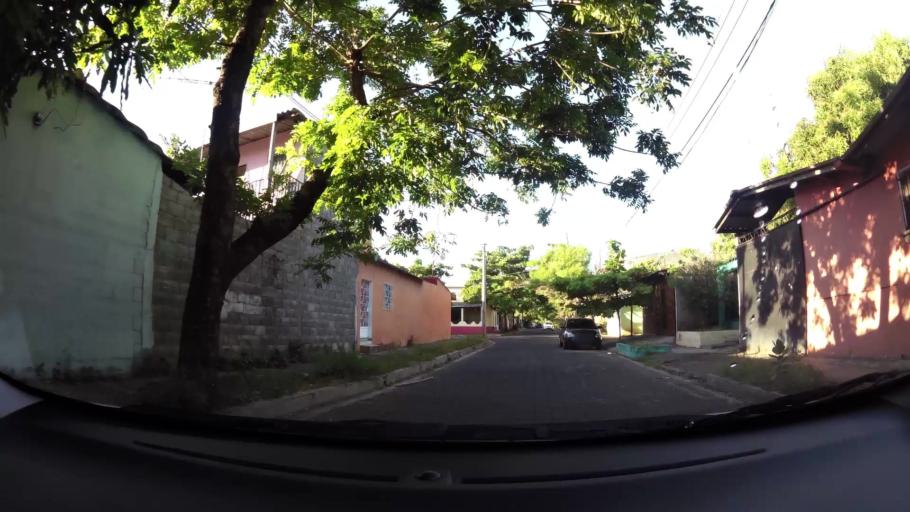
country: SV
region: San Miguel
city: San Miguel
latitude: 13.4577
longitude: -88.1633
